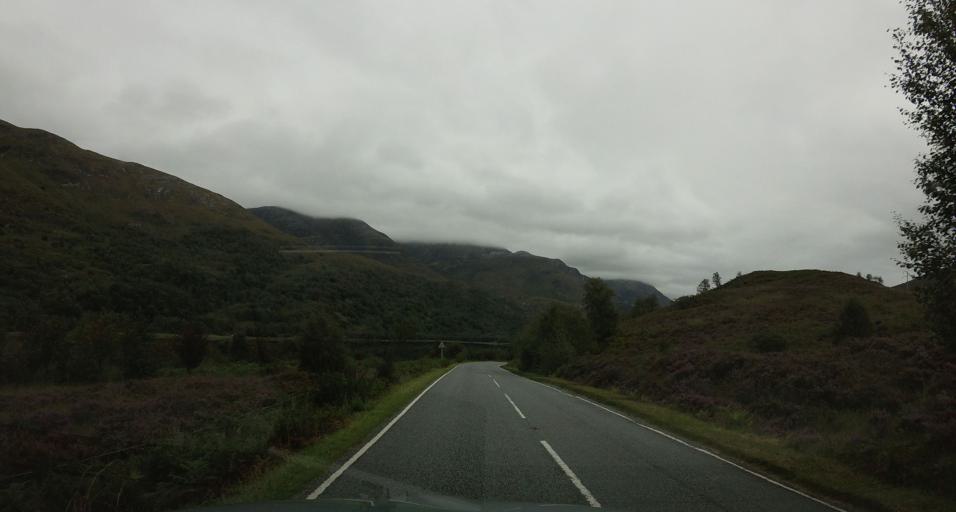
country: GB
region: Scotland
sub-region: Highland
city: Fort William
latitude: 56.7051
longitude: -5.0256
